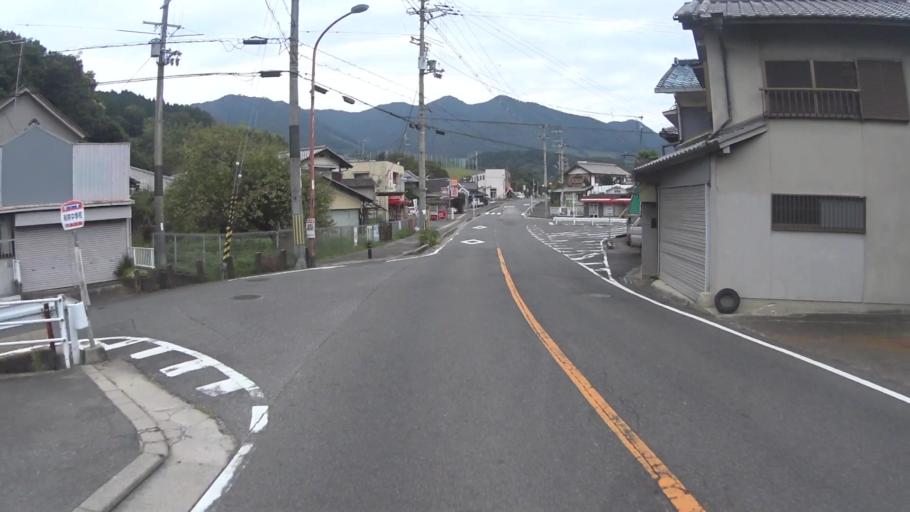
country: JP
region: Kyoto
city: Uji
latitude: 34.8003
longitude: 135.9085
